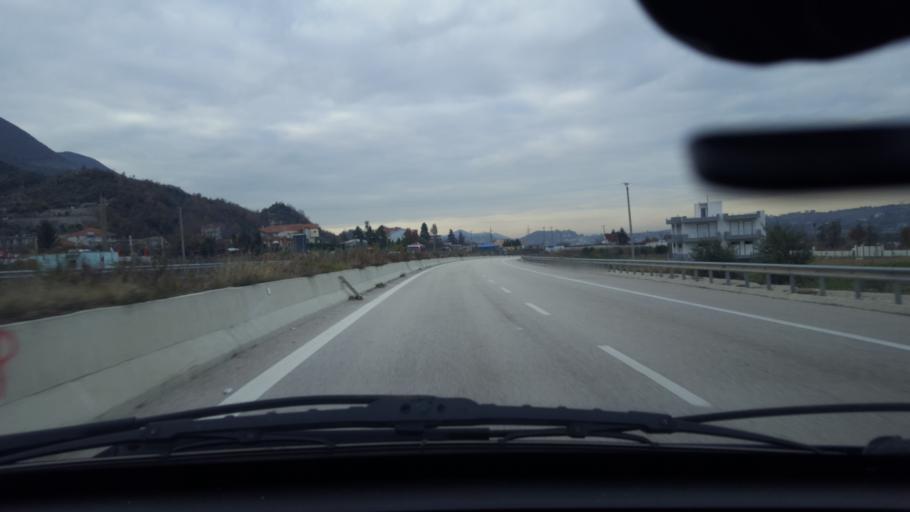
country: AL
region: Tirane
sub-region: Rrethi i Tiranes
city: Berzhite
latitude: 41.2503
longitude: 19.8988
